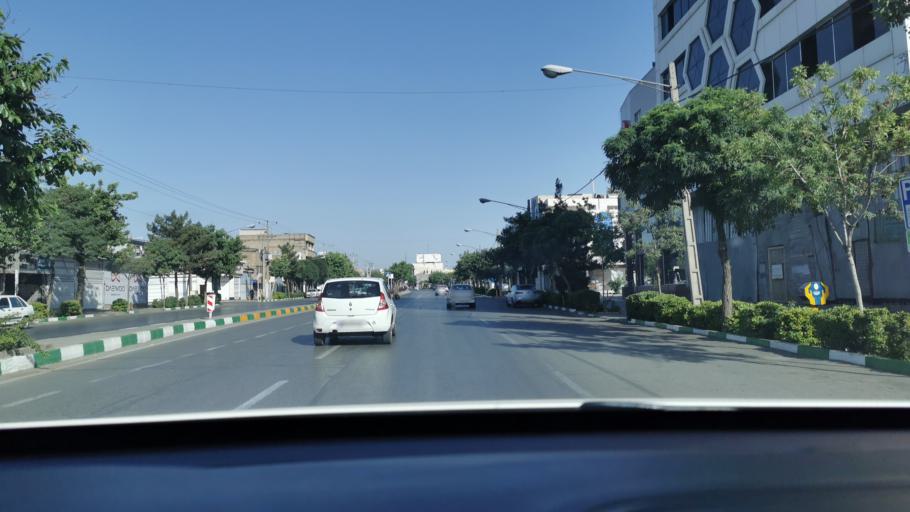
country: IR
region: Razavi Khorasan
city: Mashhad
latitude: 36.3329
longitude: 59.5144
